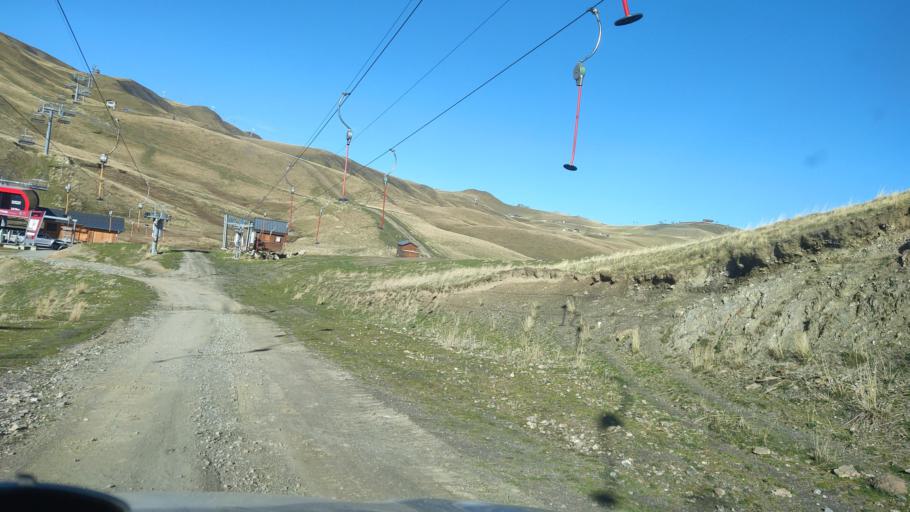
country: FR
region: Rhone-Alpes
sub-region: Departement de la Savoie
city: Saint-Etienne-de-Cuines
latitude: 45.2391
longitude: 6.2322
